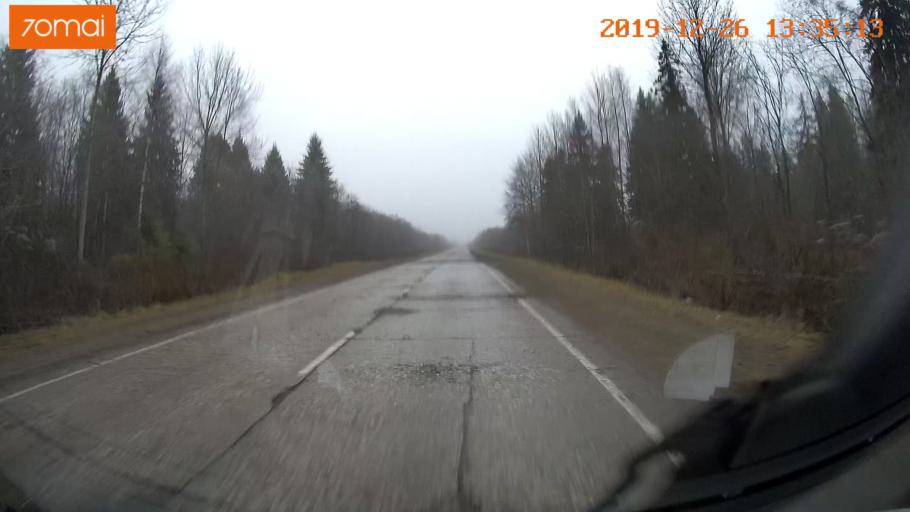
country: RU
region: Vologda
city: Sheksna
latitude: 58.7962
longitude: 38.3365
